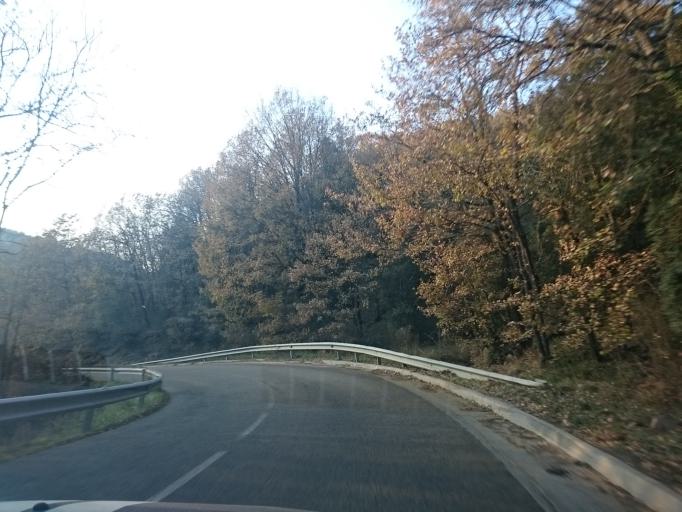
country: ES
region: Catalonia
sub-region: Provincia de Girona
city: Viladrau
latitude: 41.8484
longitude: 2.3735
